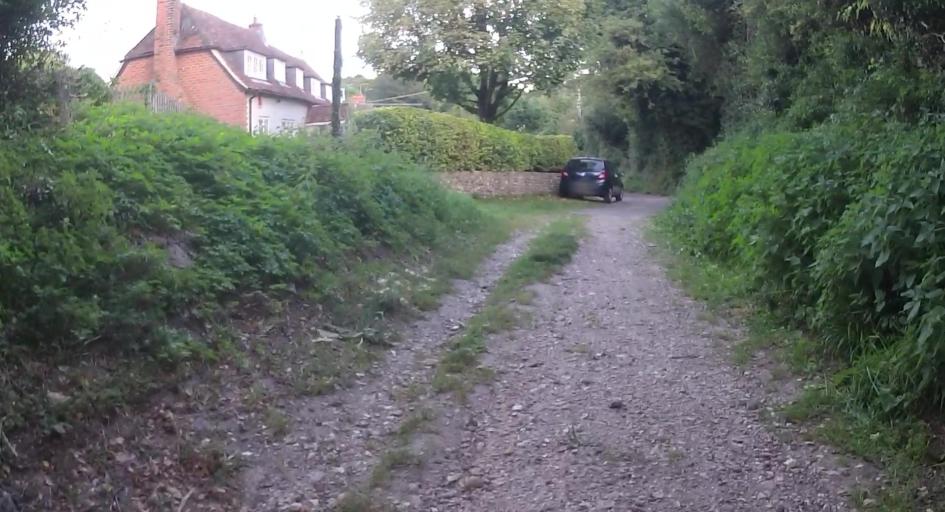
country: GB
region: England
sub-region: Hampshire
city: Four Marks
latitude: 51.1018
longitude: -1.1656
